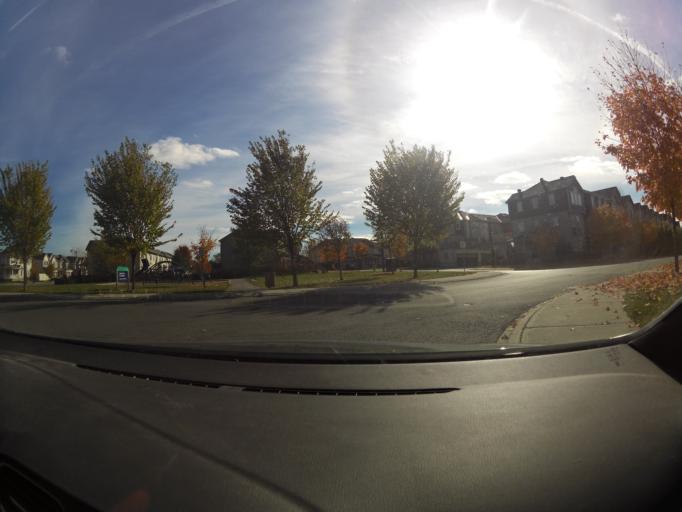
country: CA
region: Ontario
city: Bells Corners
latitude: 45.2879
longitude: -75.9260
